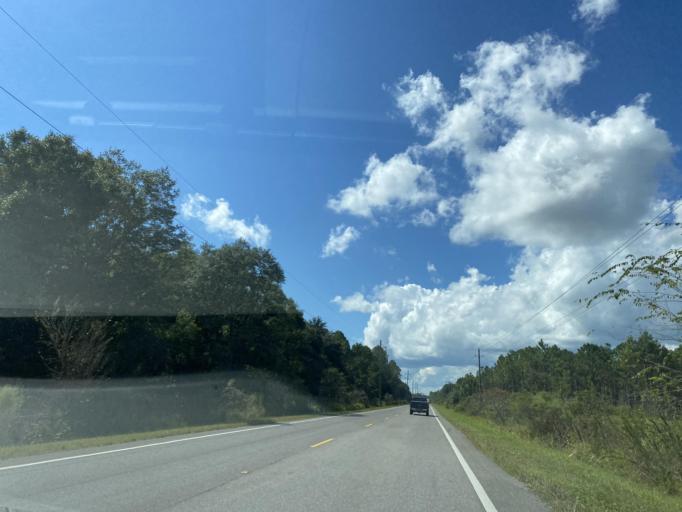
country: US
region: Florida
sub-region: Lake County
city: Umatilla
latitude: 28.9603
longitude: -81.6068
